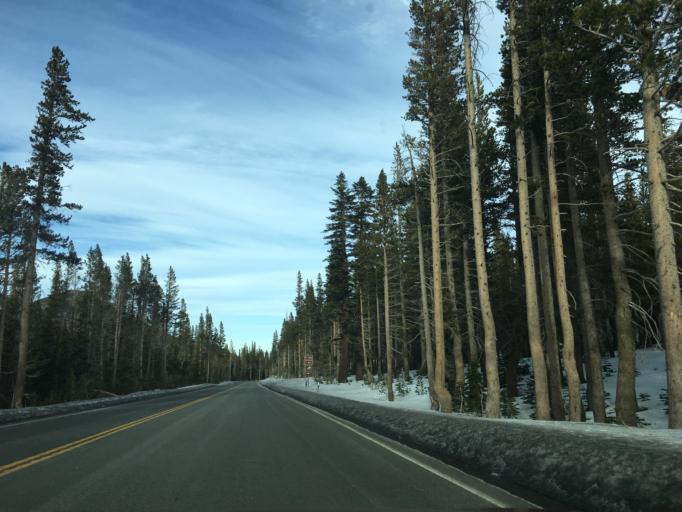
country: US
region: Nevada
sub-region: Washoe County
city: Incline Village
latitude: 39.3251
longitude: -119.8927
